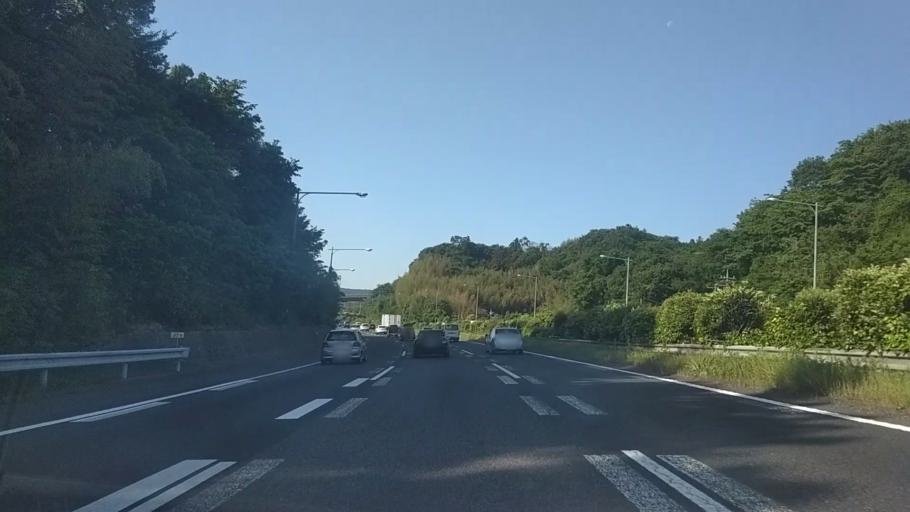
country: JP
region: Kanagawa
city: Hadano
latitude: 35.3484
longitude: 139.2050
